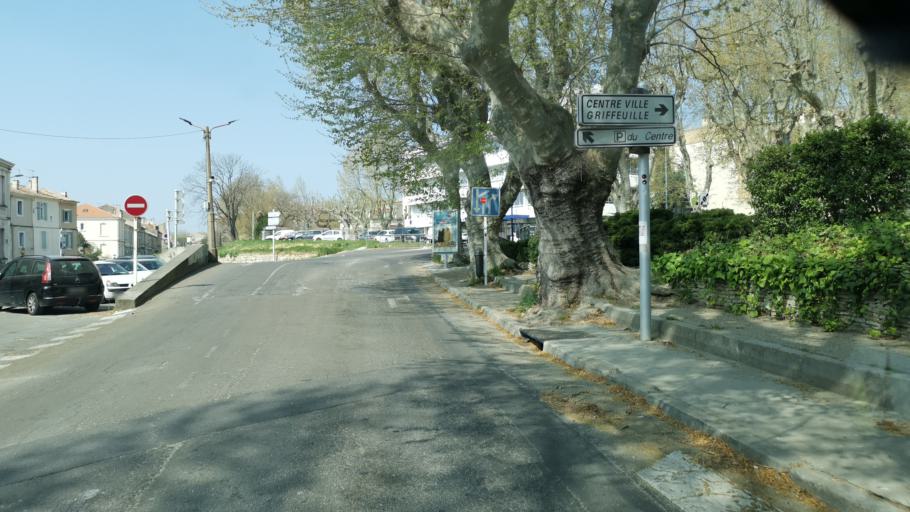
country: FR
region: Provence-Alpes-Cote d'Azur
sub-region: Departement des Bouches-du-Rhone
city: Arles
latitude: 43.6735
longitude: 4.6326
